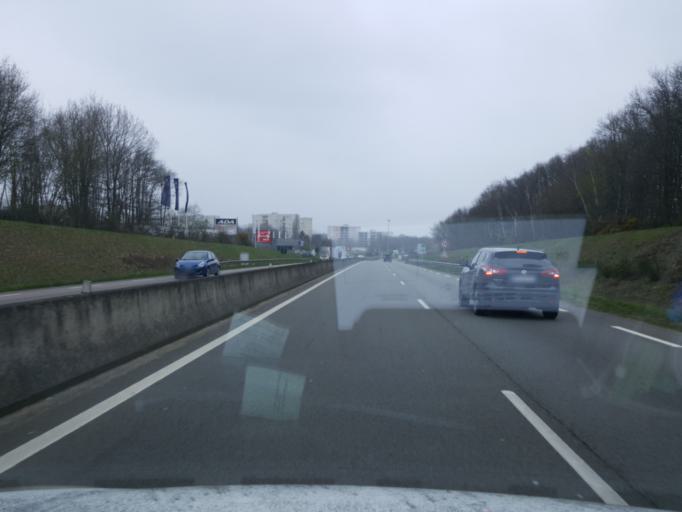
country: FR
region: Centre
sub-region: Departement d'Eure-et-Loir
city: Dreux
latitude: 48.7281
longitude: 1.3442
